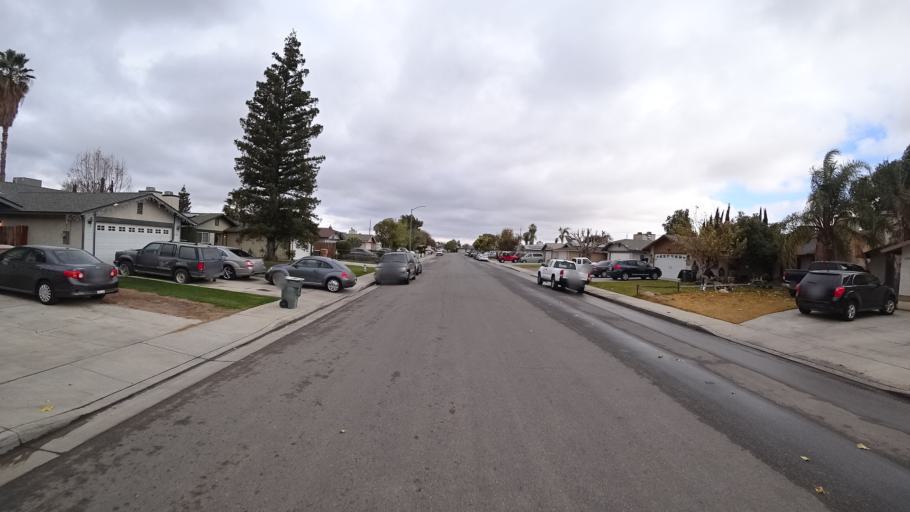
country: US
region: California
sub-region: Kern County
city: Greenfield
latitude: 35.2937
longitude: -119.0168
